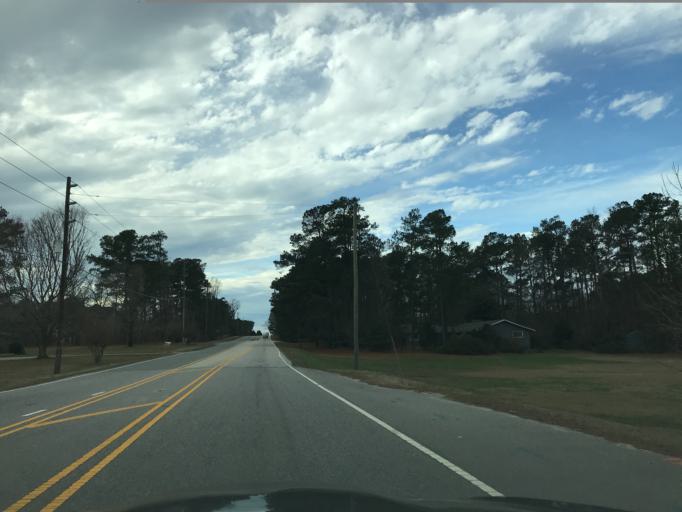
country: US
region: North Carolina
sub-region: Wake County
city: Knightdale
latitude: 35.8561
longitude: -78.5590
